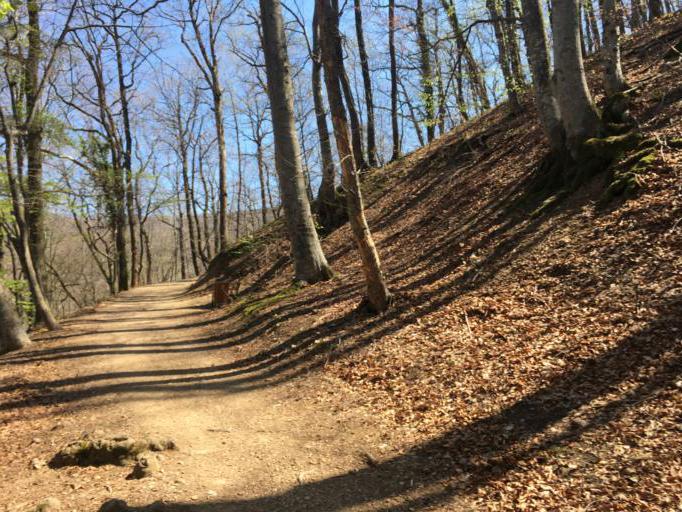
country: XK
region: Pristina
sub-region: Komuna e Prishtines
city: Pristina
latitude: 42.6658
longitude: 21.2189
